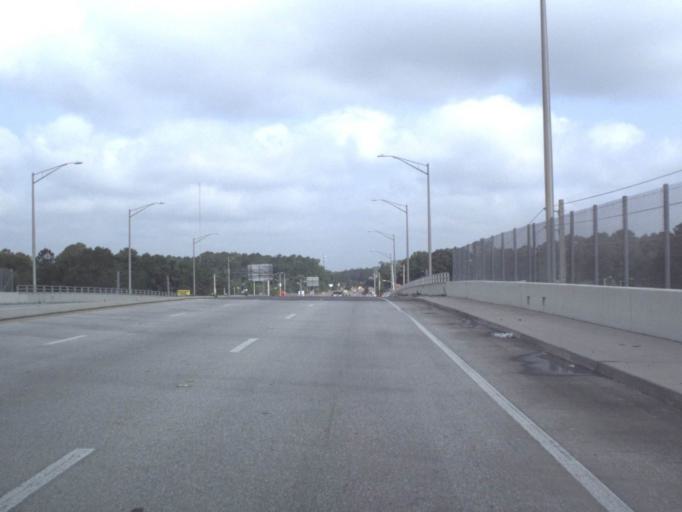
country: US
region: Florida
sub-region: Duval County
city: Jacksonville
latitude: 30.3607
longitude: -81.7140
